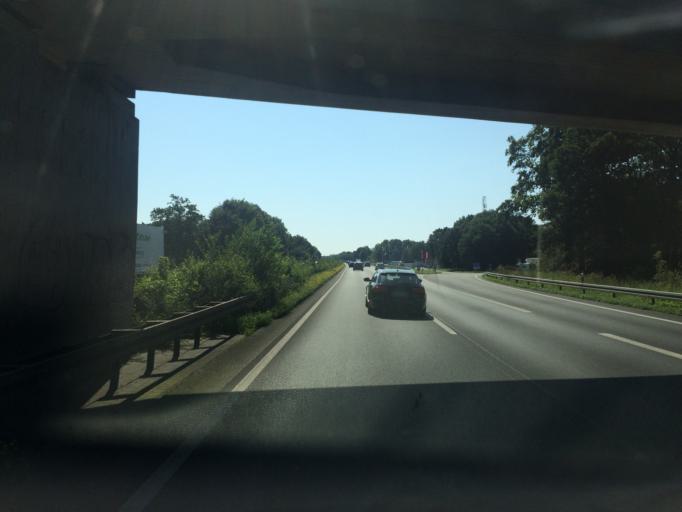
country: DE
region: North Rhine-Westphalia
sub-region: Regierungsbezirk Munster
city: Ascheberg
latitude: 51.7763
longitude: 7.6395
